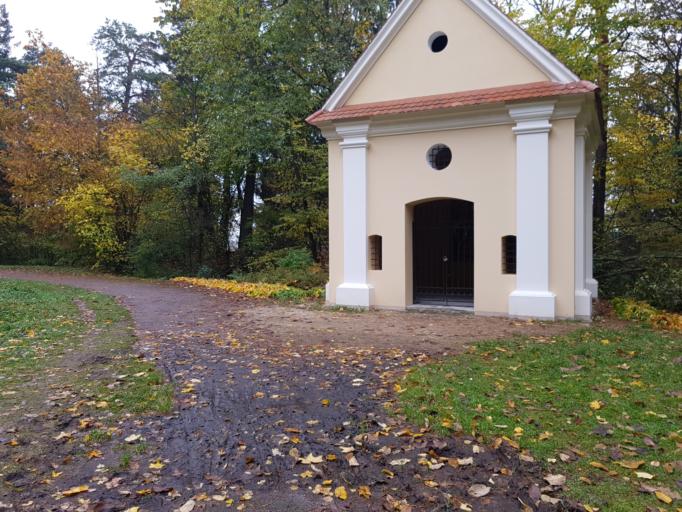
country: LT
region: Vilnius County
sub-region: Vilnius
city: Vilnius
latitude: 54.7291
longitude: 25.2877
